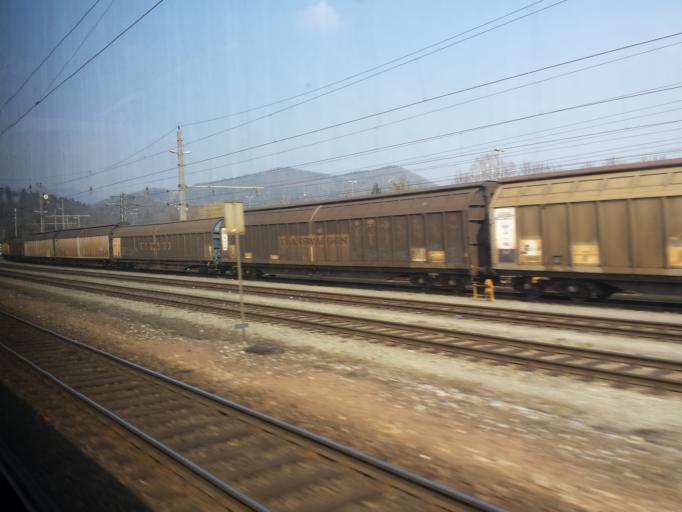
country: AT
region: Styria
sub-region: Politischer Bezirk Graz-Umgebung
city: Gratwein
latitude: 47.1270
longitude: 15.3266
